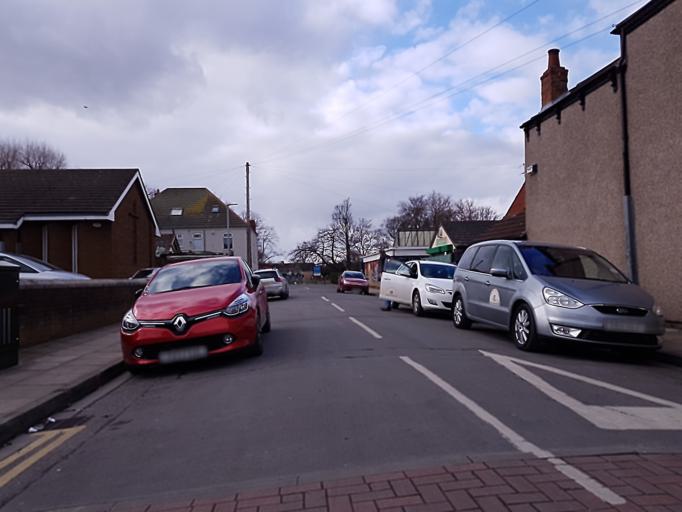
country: GB
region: England
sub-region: North East Lincolnshire
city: Grimsby
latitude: 53.5667
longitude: -0.0626
